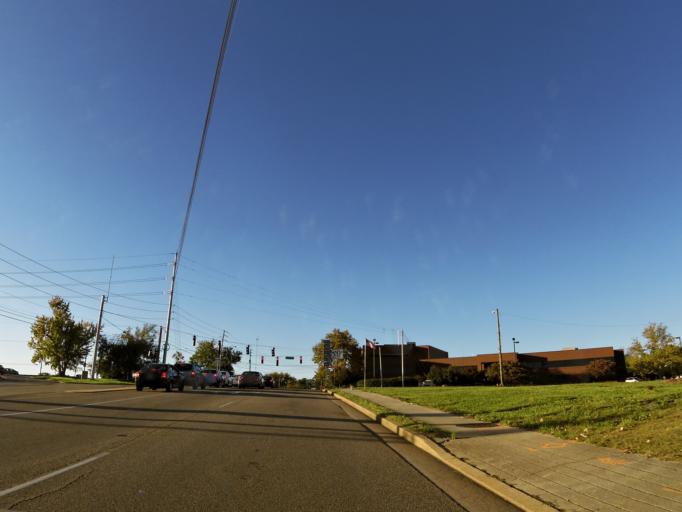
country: US
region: Tennessee
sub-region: Knox County
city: Knoxville
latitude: 35.9648
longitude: -83.9367
